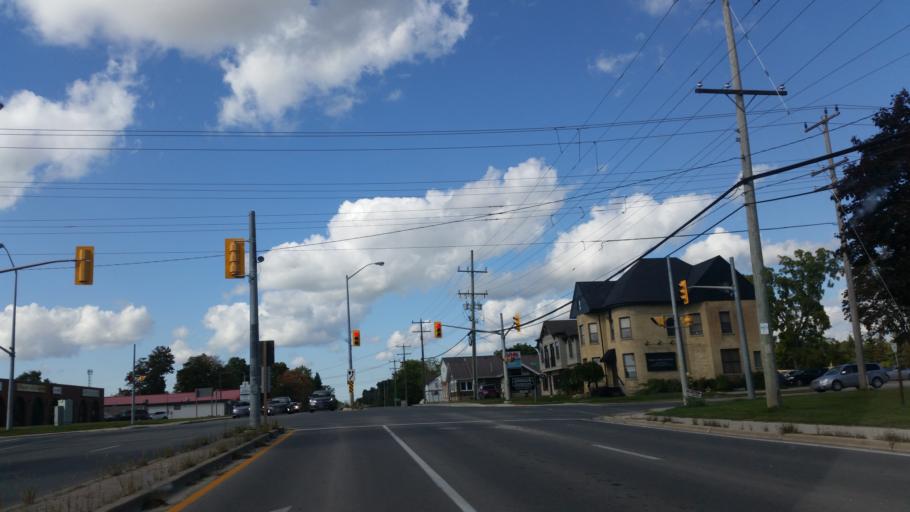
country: CA
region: Ontario
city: London
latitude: 43.0501
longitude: -81.2947
